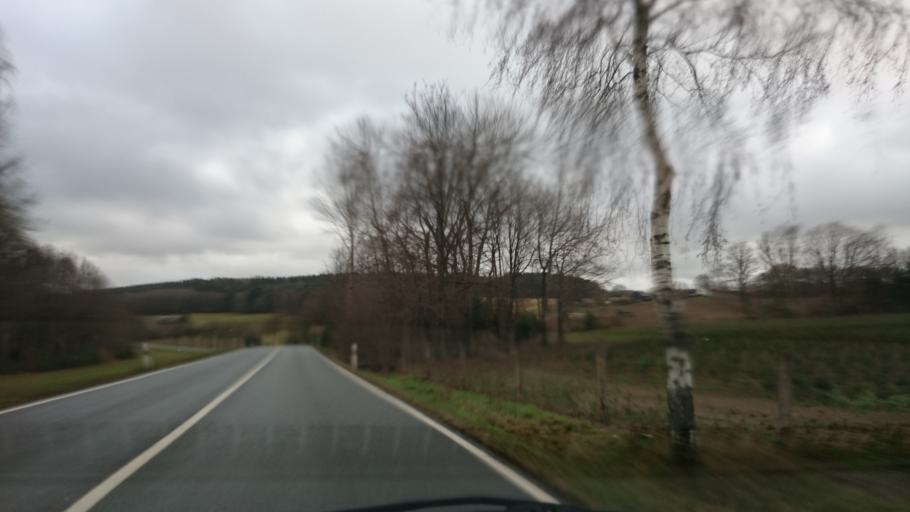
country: DE
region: Saxony
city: Kirchberg
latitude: 50.6351
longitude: 12.5660
